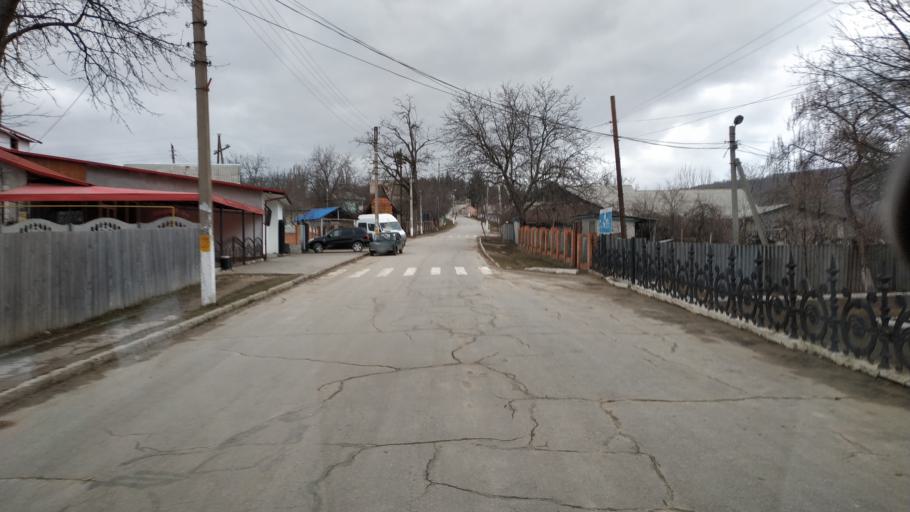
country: MD
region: Calarasi
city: Calarasi
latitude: 47.2643
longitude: 28.1323
